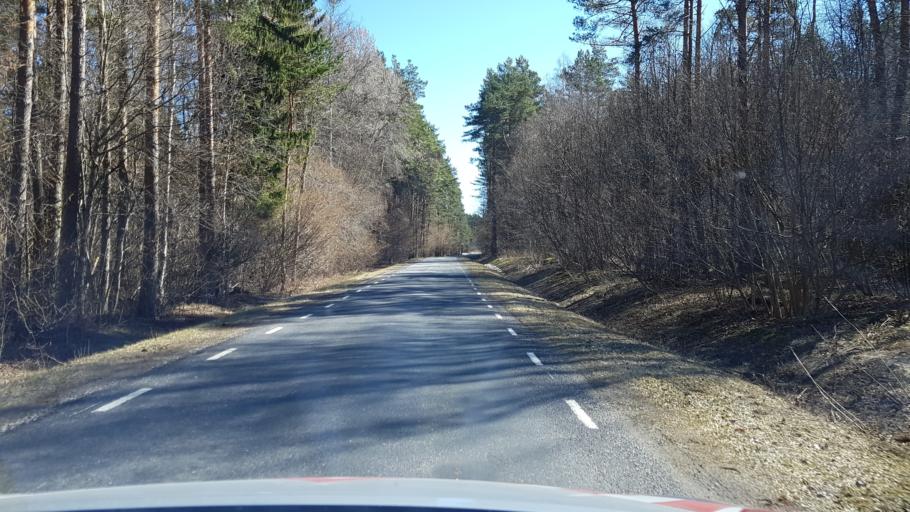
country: EE
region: Laeaene-Virumaa
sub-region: Viru-Nigula vald
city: Kunda
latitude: 59.5304
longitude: 26.4405
